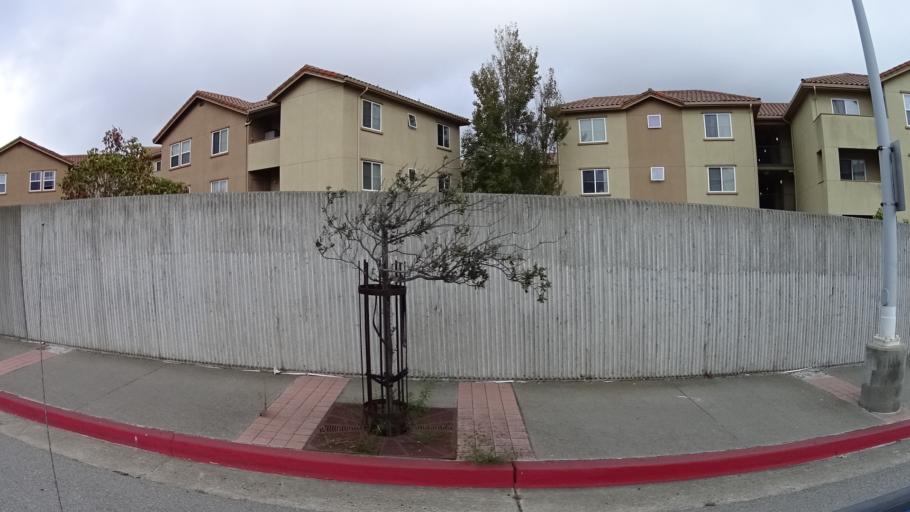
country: US
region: California
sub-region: San Mateo County
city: Colma
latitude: 37.6847
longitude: -122.4650
